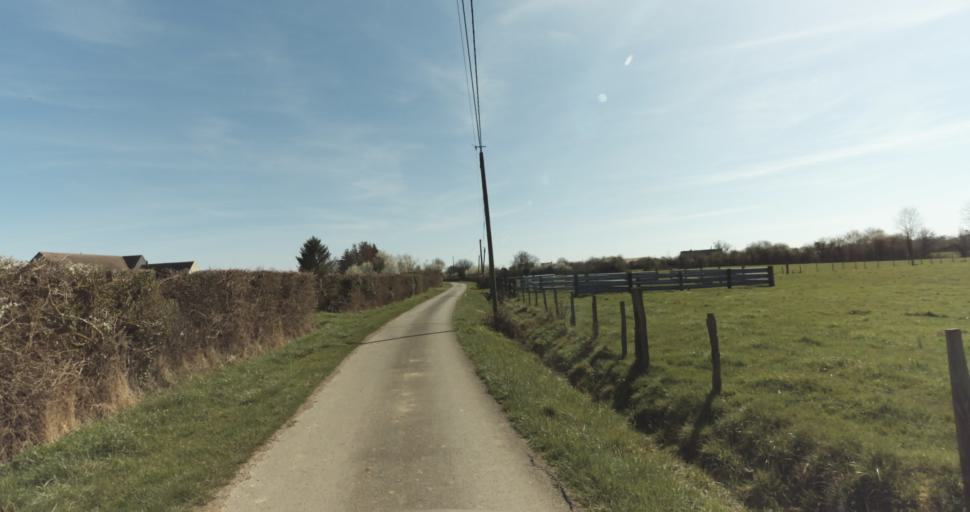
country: FR
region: Lower Normandy
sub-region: Departement du Calvados
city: Saint-Pierre-sur-Dives
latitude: 49.0538
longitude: -0.0346
